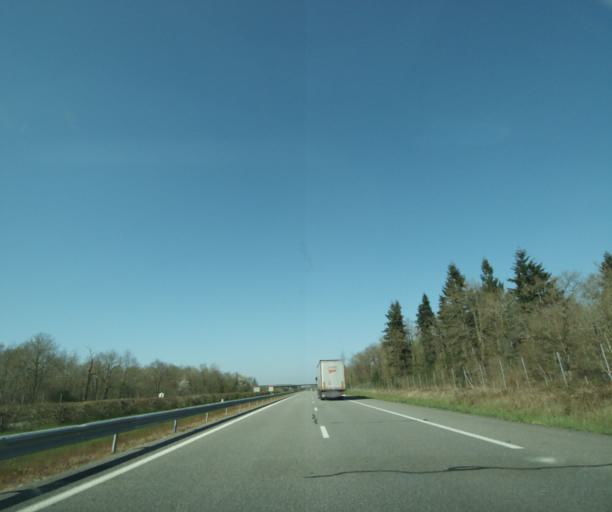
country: FR
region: Centre
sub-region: Departement du Loiret
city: Briare
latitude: 47.6933
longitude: 2.7398
